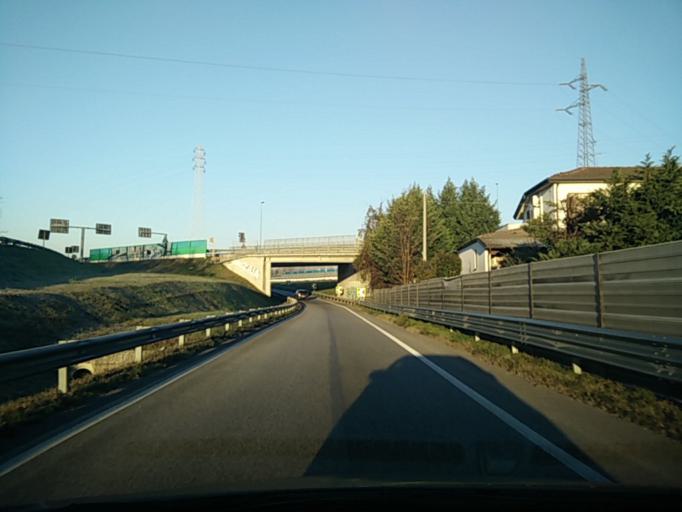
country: IT
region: Veneto
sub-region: Provincia di Treviso
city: Silea
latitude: 45.6559
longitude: 12.2851
